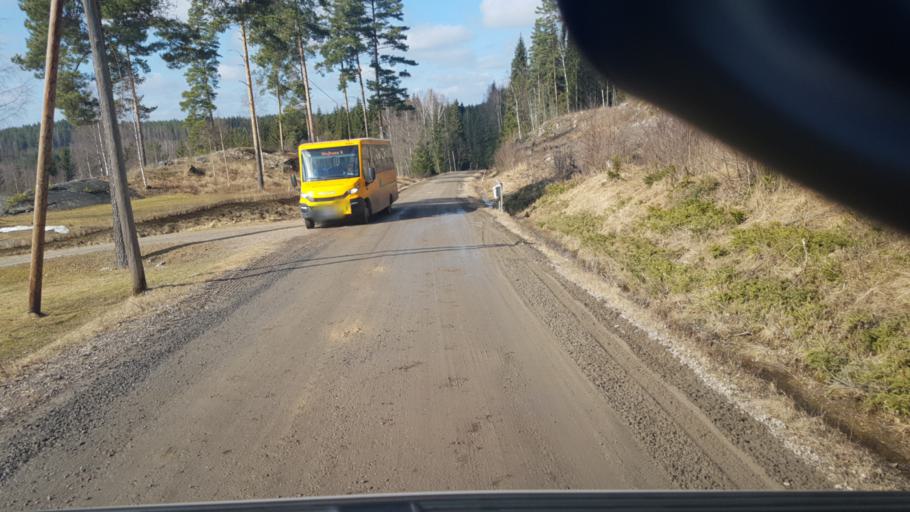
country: SE
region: Vaermland
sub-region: Eda Kommun
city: Amotfors
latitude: 59.8218
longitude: 12.4501
